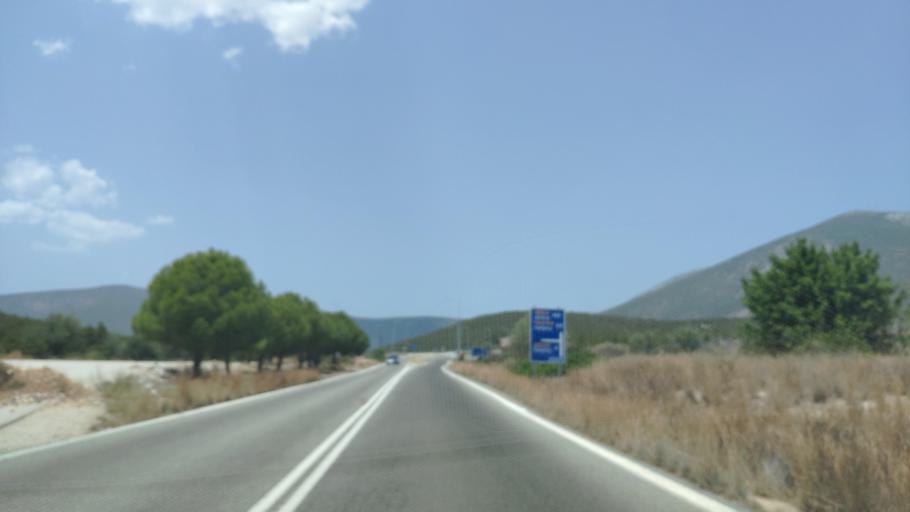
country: GR
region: Peloponnese
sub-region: Nomos Argolidos
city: Didyma
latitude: 37.4413
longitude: 23.1858
